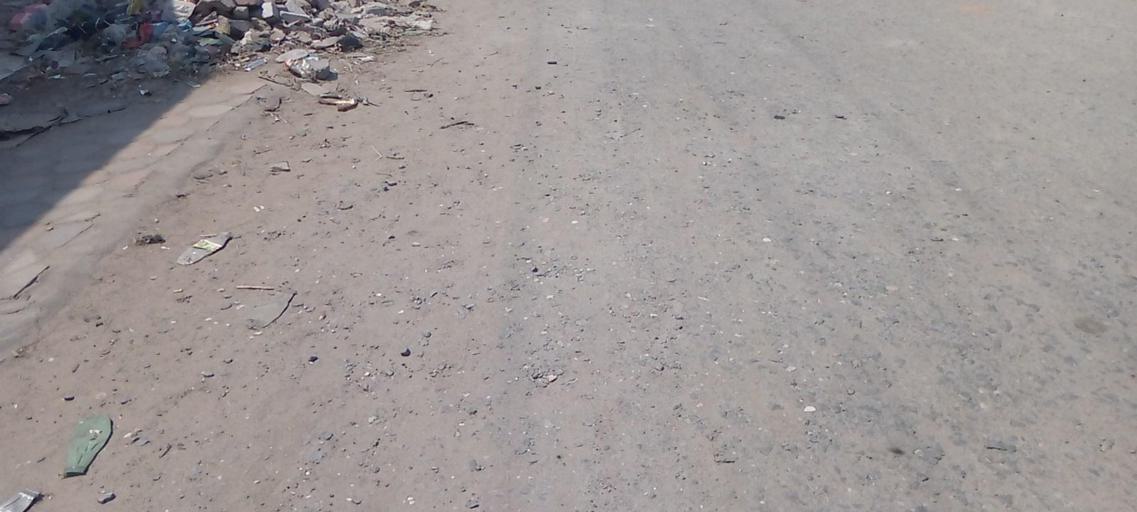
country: ZM
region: Lusaka
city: Lusaka
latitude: -15.4039
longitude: 28.3561
